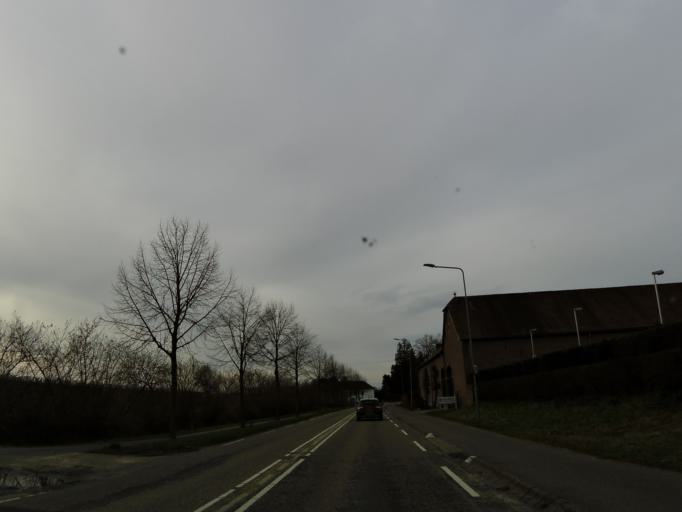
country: NL
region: Limburg
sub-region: Gemeente Voerendaal
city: Klimmen
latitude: 50.8754
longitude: 5.8593
